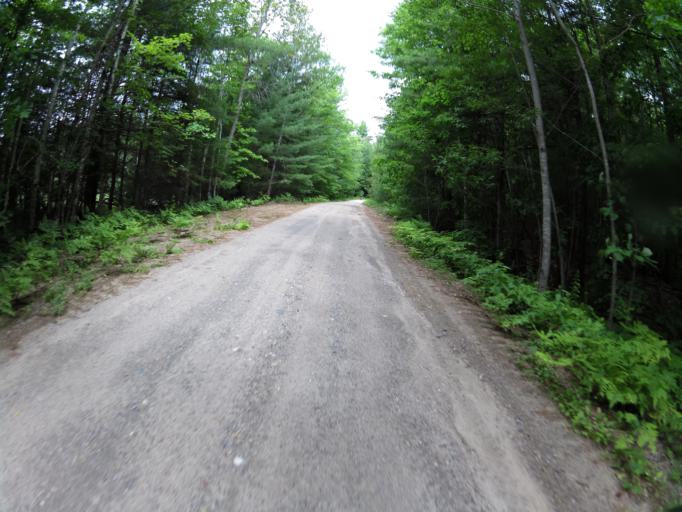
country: CA
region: Ontario
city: Perth
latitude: 45.0115
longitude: -76.5966
